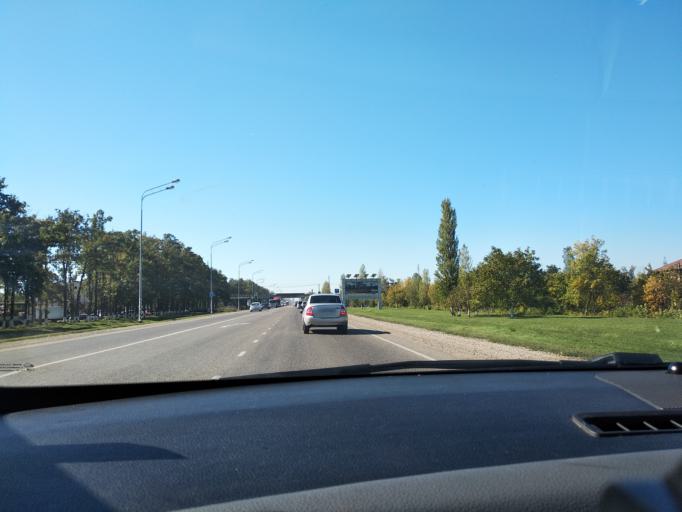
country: RU
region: Krasnodarskiy
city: Krasnodar
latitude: 45.1380
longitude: 39.0336
